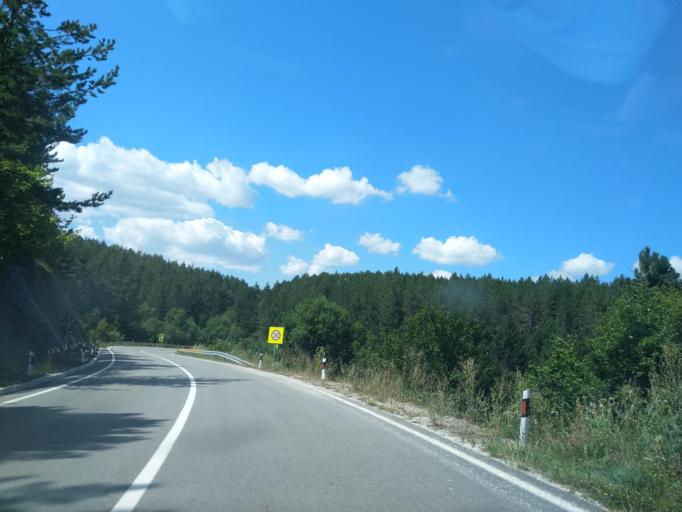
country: RS
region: Central Serbia
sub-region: Zlatiborski Okrug
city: Sjenica
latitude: 43.3071
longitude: 19.8999
